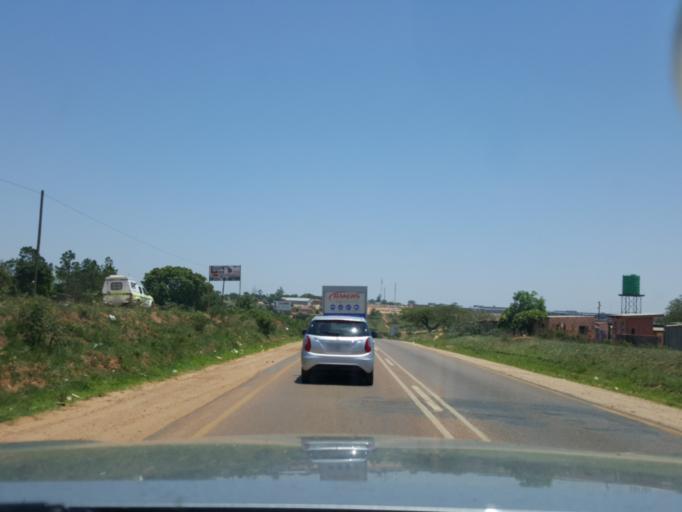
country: ZA
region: Limpopo
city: Thulamahashi
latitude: -24.6177
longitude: 31.0392
